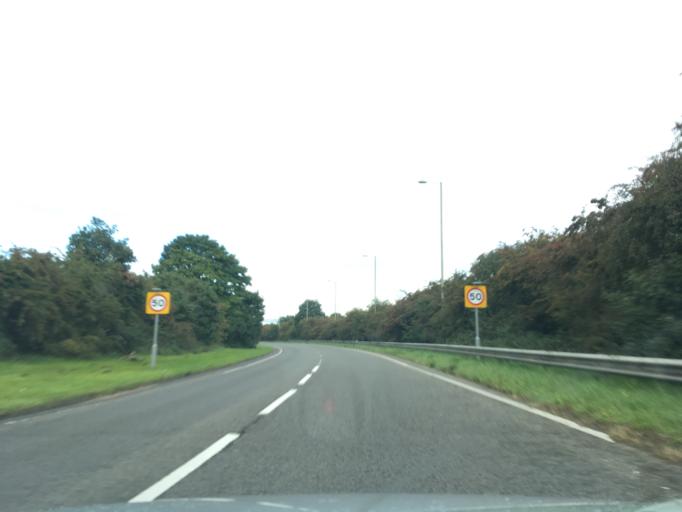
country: GB
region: England
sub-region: Oxfordshire
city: Cowley
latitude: 51.7642
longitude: -1.1981
